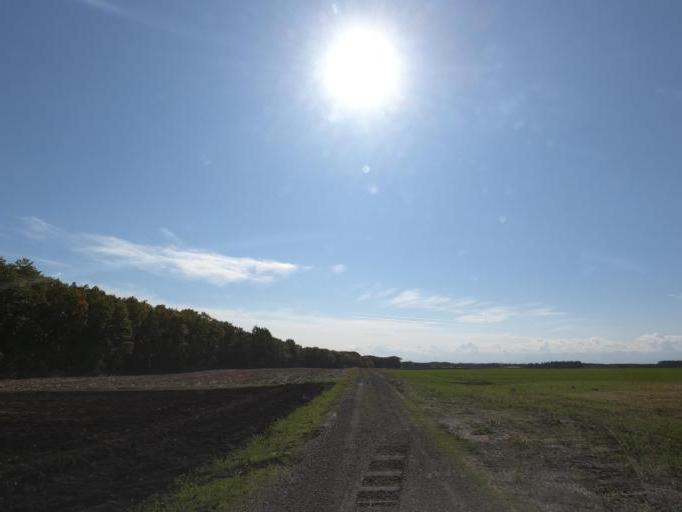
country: JP
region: Hokkaido
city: Otofuke
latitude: 43.2389
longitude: 143.2621
